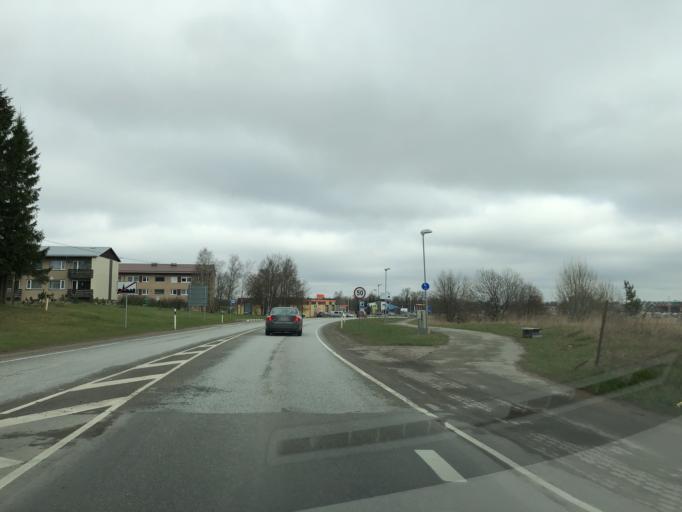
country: EE
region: Laeaene-Virumaa
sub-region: Rakvere linn
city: Rakvere
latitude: 59.3596
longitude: 26.3346
